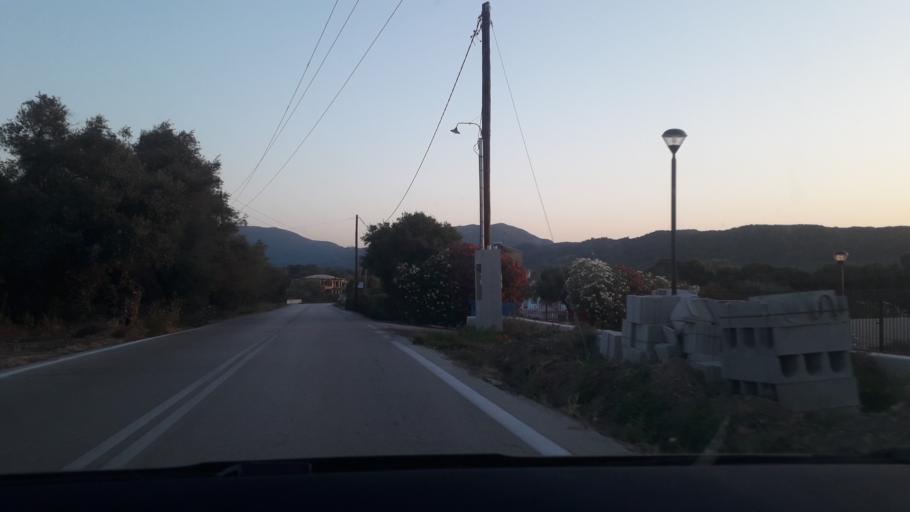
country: GR
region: Ionian Islands
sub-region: Nomos Kerkyras
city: Agios Matthaios
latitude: 39.4698
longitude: 19.9115
